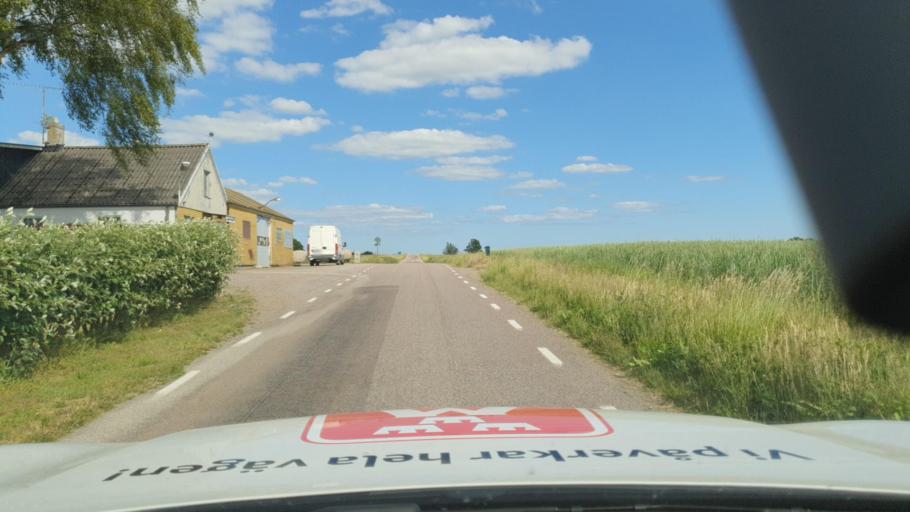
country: SE
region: Skane
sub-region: Ystads Kommun
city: Kopingebro
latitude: 55.4709
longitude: 13.9524
